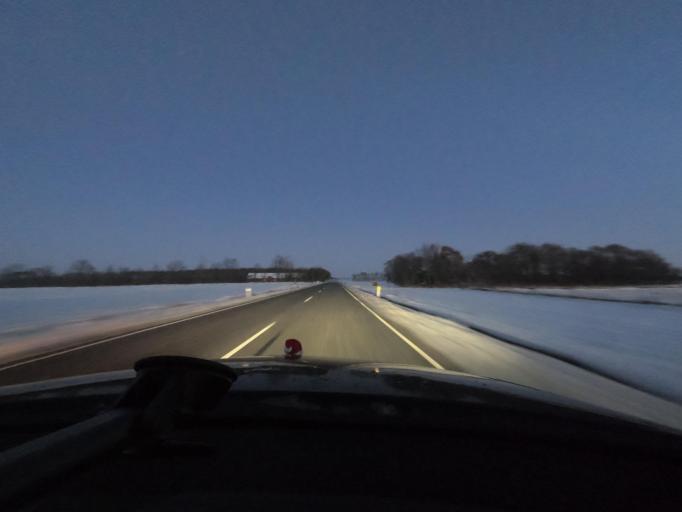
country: DK
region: South Denmark
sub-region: Tonder Kommune
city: Sherrebek
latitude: 55.1758
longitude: 8.8760
